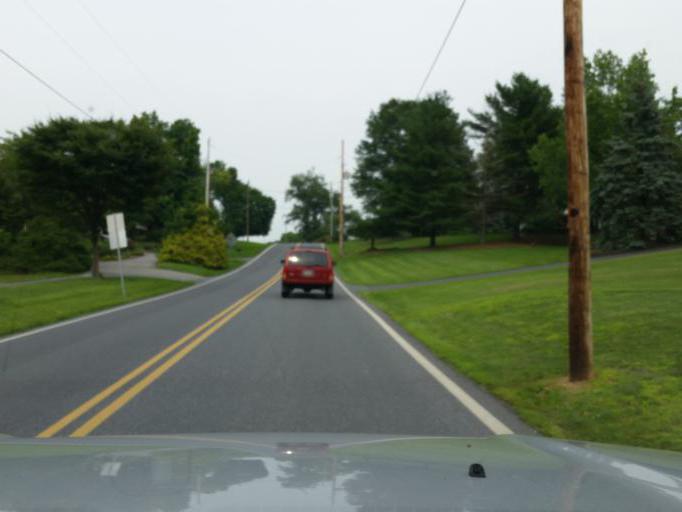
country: US
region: Pennsylvania
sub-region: Lancaster County
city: Manheim
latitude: 40.1476
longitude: -76.4049
